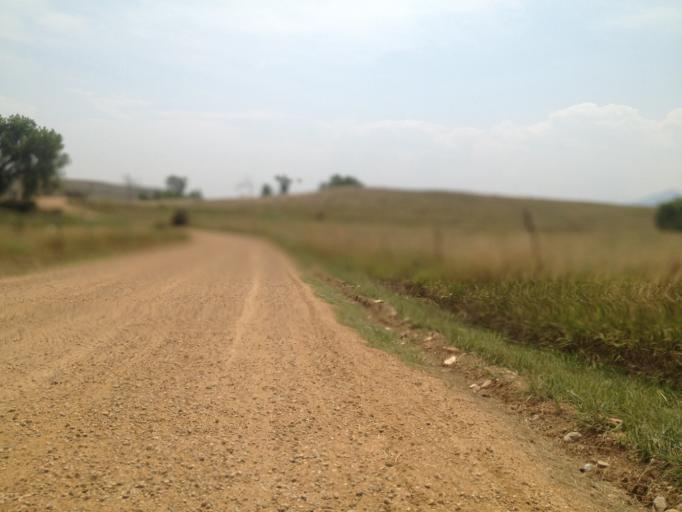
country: US
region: Colorado
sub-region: Boulder County
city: Superior
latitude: 39.9481
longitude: -105.1850
